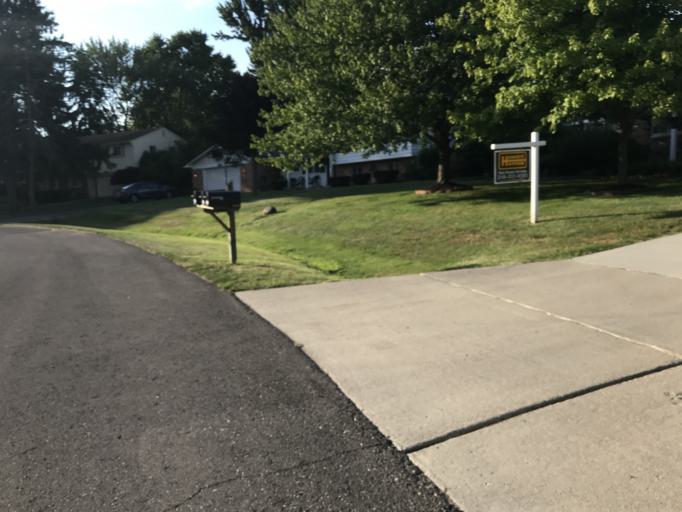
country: US
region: Michigan
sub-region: Oakland County
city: Farmington Hills
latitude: 42.4908
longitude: -83.3435
